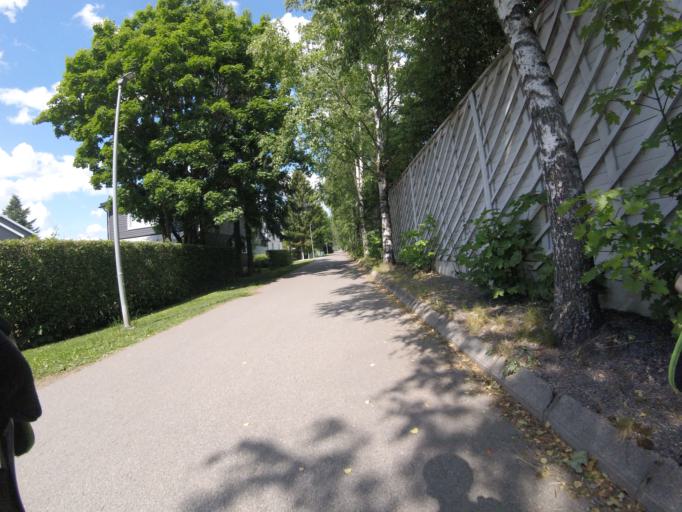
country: NO
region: Akershus
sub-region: Skedsmo
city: Lillestrom
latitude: 59.9580
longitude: 11.0687
